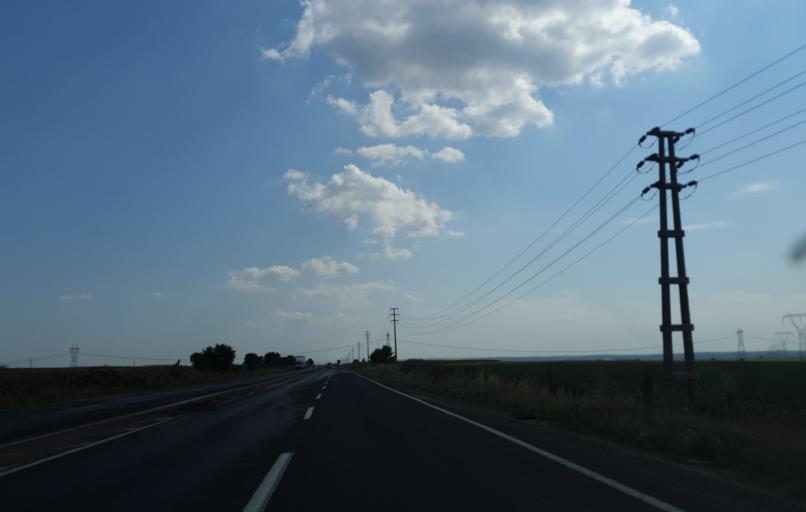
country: TR
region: Kirklareli
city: Buyukkaristiran
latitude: 41.2405
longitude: 27.5373
